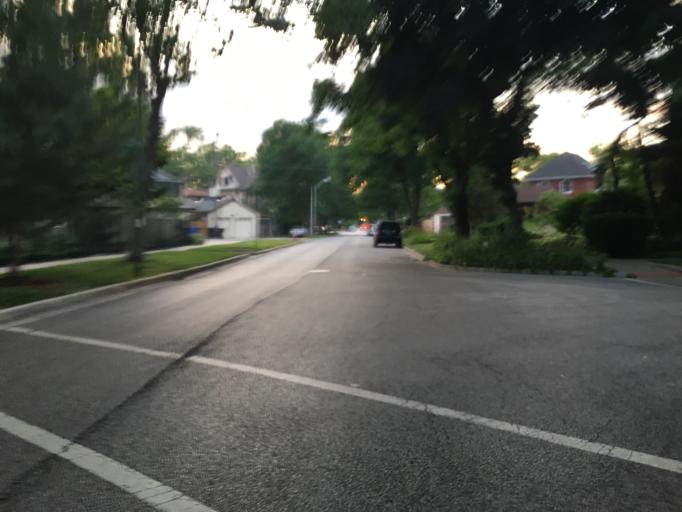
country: US
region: Illinois
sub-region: Cook County
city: Lincolnwood
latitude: 41.9639
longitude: -87.6987
